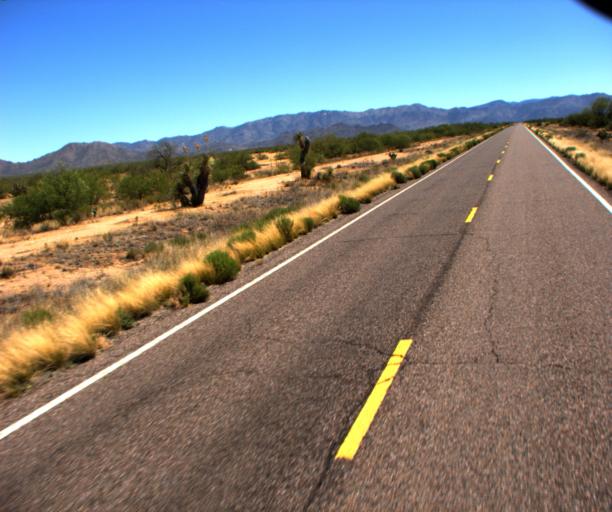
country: US
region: Arizona
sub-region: Yavapai County
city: Congress
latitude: 34.1397
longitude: -112.9094
